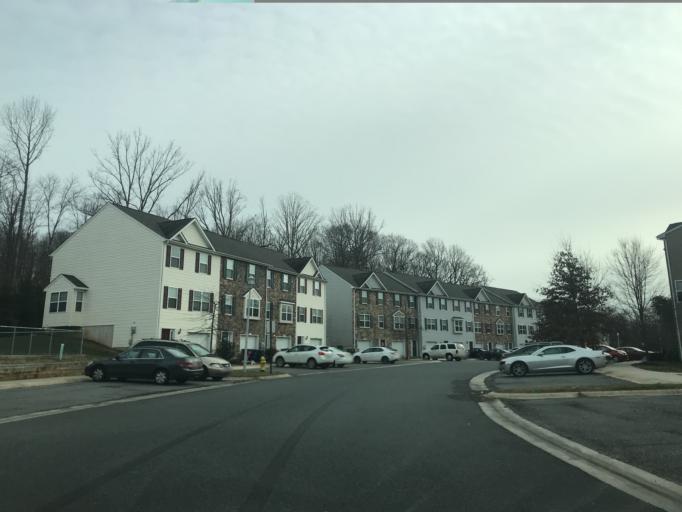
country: US
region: Maryland
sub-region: Cecil County
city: Elkton
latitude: 39.6148
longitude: -75.8054
